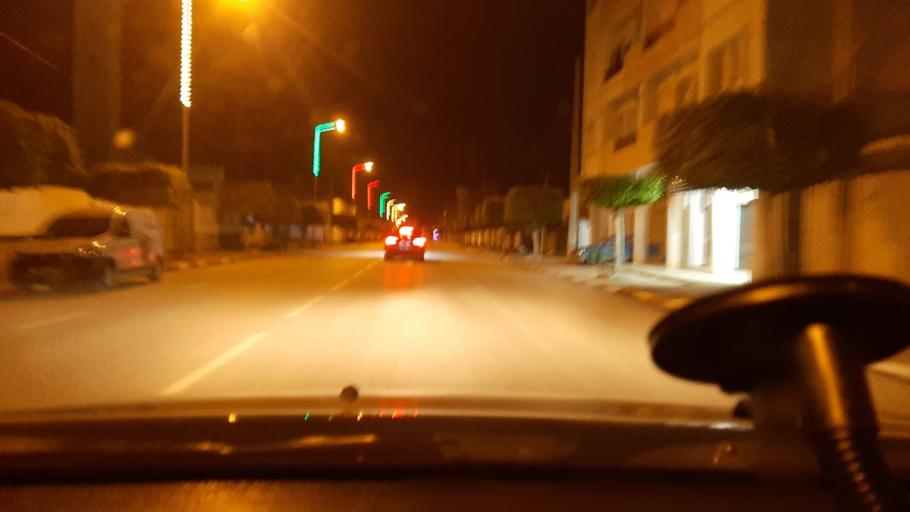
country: TN
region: Safaqis
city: Sfax
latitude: 34.7771
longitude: 10.7269
